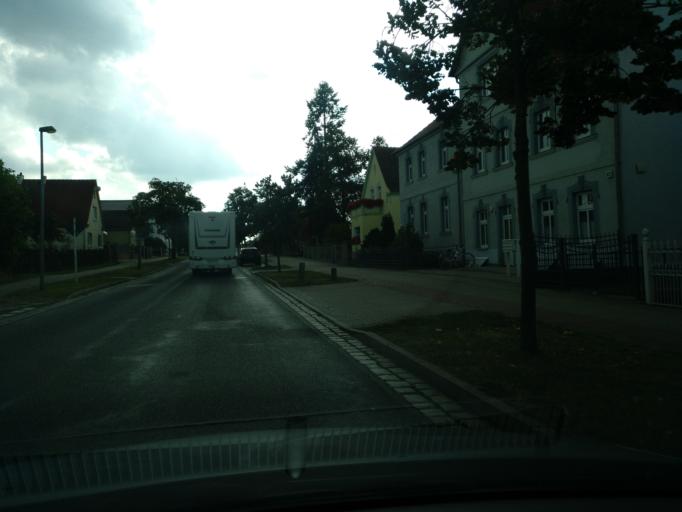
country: DE
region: Brandenburg
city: Woltersdorf
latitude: 52.4771
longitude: 13.7735
